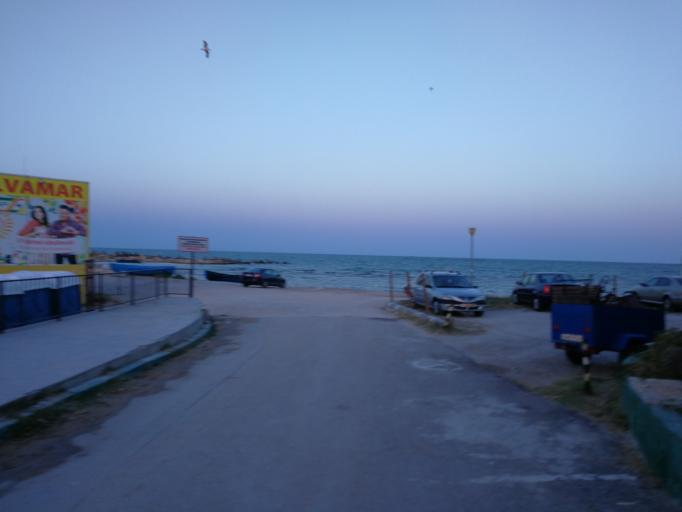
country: RO
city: Eforie Sud
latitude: 44.0278
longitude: 28.6568
